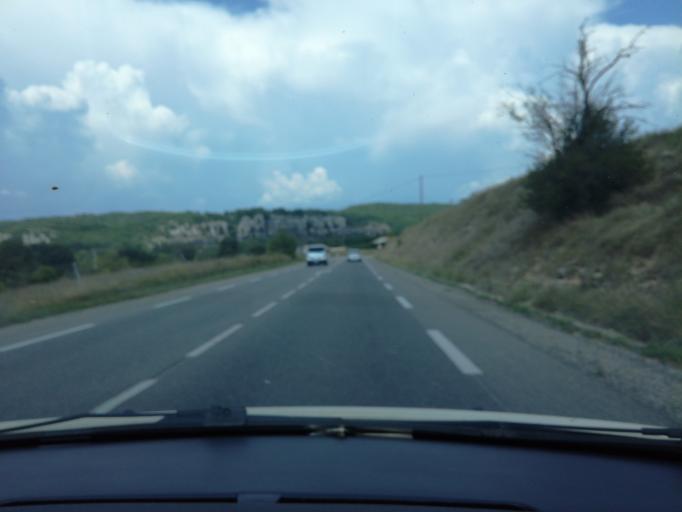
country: FR
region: Rhone-Alpes
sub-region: Departement de l'Ardeche
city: Lachapelle-sous-Aubenas
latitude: 44.5075
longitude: 4.3858
